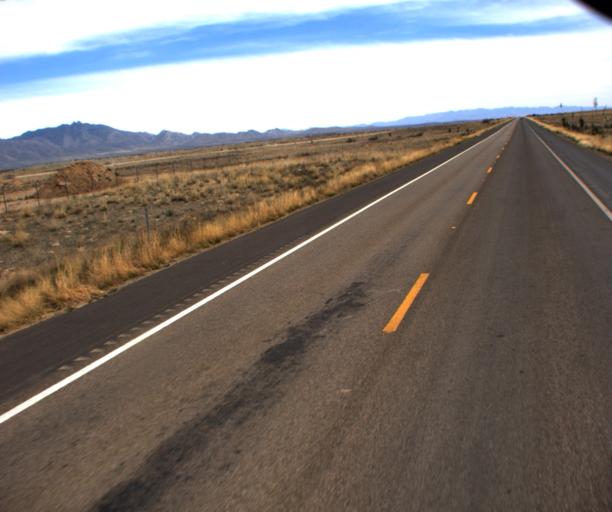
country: US
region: Arizona
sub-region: Cochise County
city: Willcox
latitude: 32.2386
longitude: -109.8109
